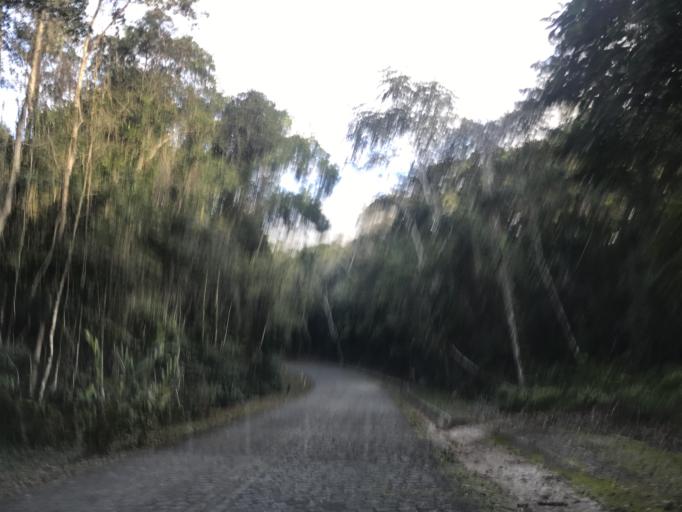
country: BR
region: Bahia
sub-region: Gandu
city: Gandu
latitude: -13.9031
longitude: -39.4617
